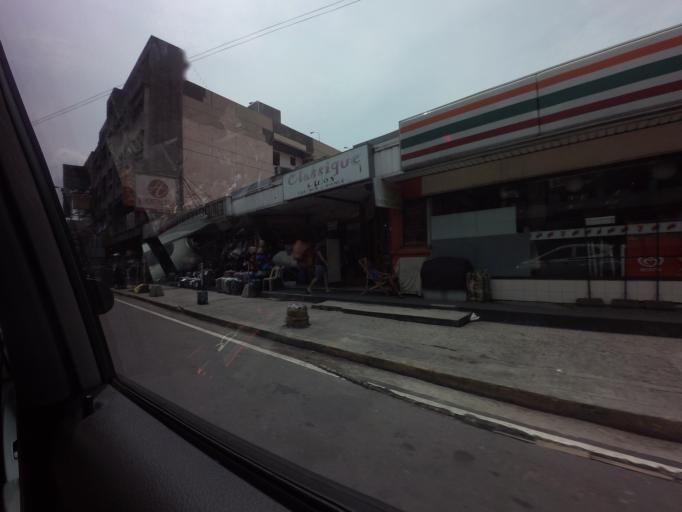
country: PH
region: Metro Manila
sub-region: City of Manila
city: Port Area
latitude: 14.5765
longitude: 120.9892
